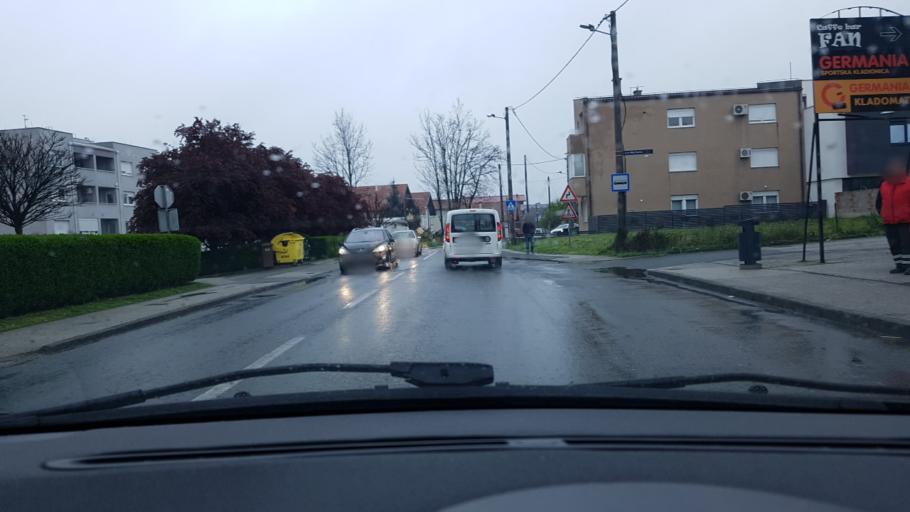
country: HR
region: Grad Zagreb
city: Dubrava
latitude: 45.8130
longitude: 16.0550
